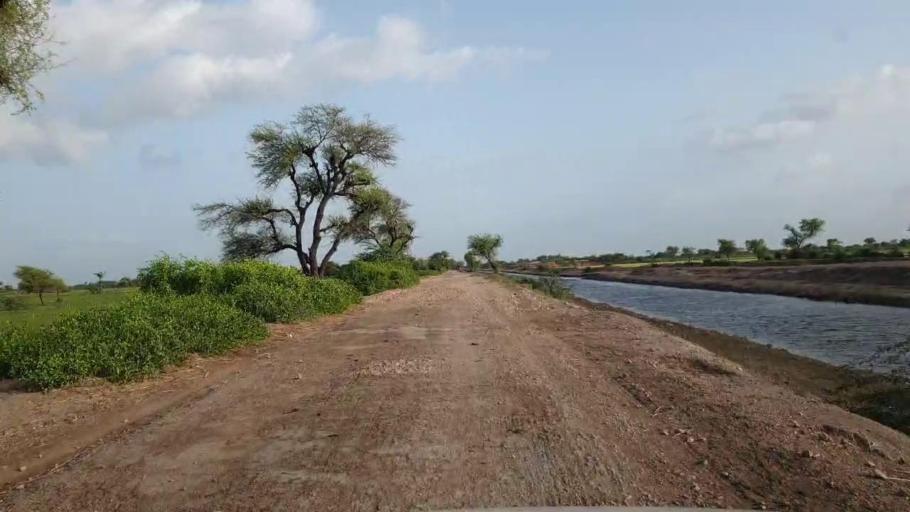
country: PK
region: Sindh
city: Kario
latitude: 24.8041
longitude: 68.6472
